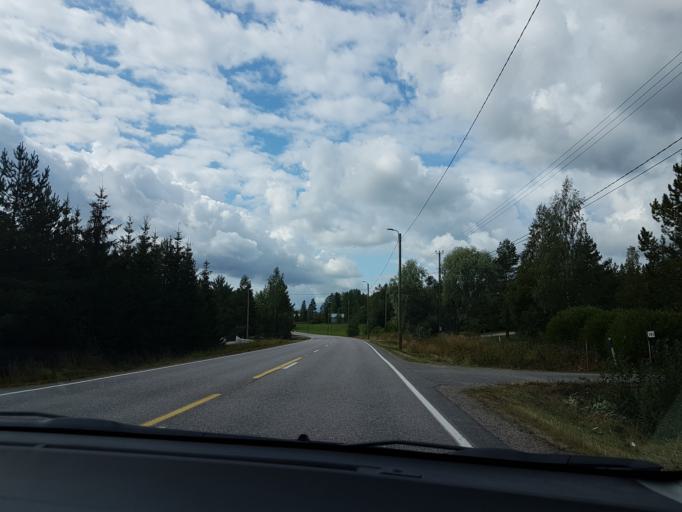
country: FI
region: Uusimaa
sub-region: Helsinki
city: Pornainen
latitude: 60.4837
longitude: 25.3437
